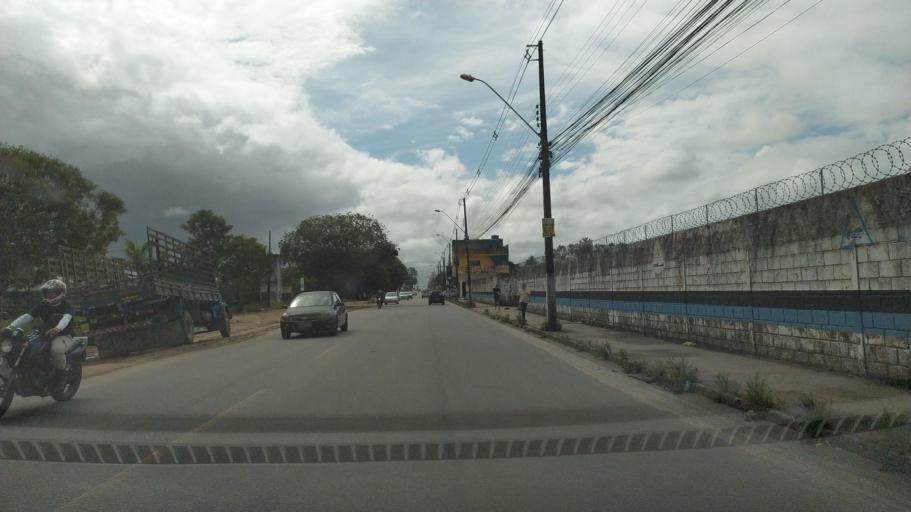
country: BR
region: Alagoas
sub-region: Satuba
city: Satuba
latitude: -9.5497
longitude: -35.7597
